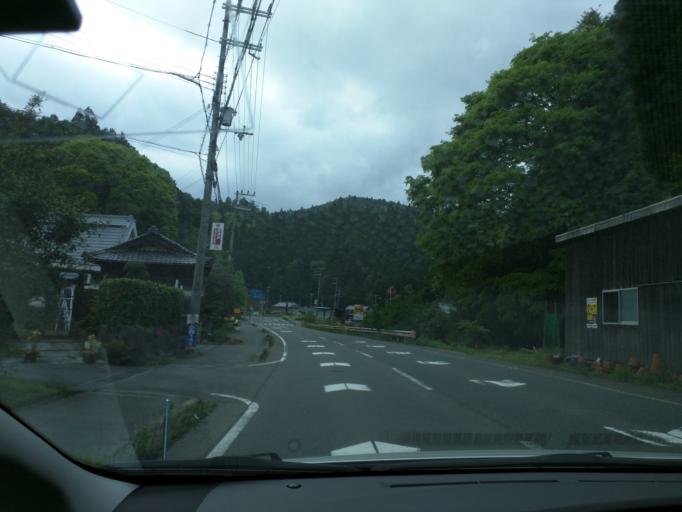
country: JP
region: Shiga Prefecture
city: Kusatsu
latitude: 34.8602
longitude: 135.9708
